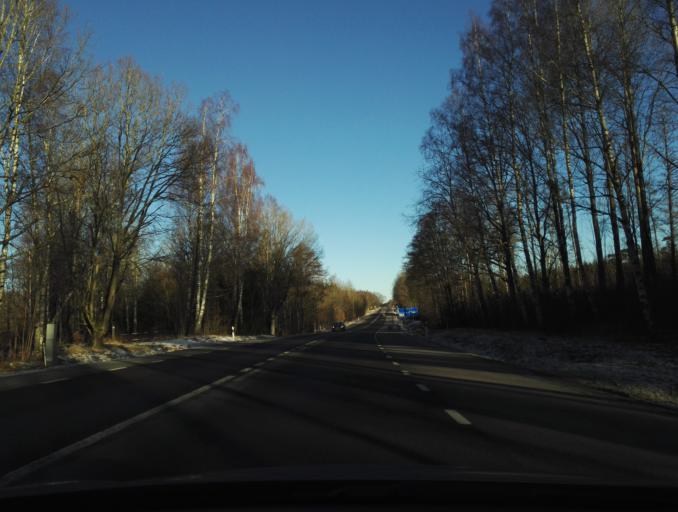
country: SE
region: Kronoberg
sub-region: Vaxjo Kommun
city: Vaexjoe
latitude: 56.8620
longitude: 14.7327
